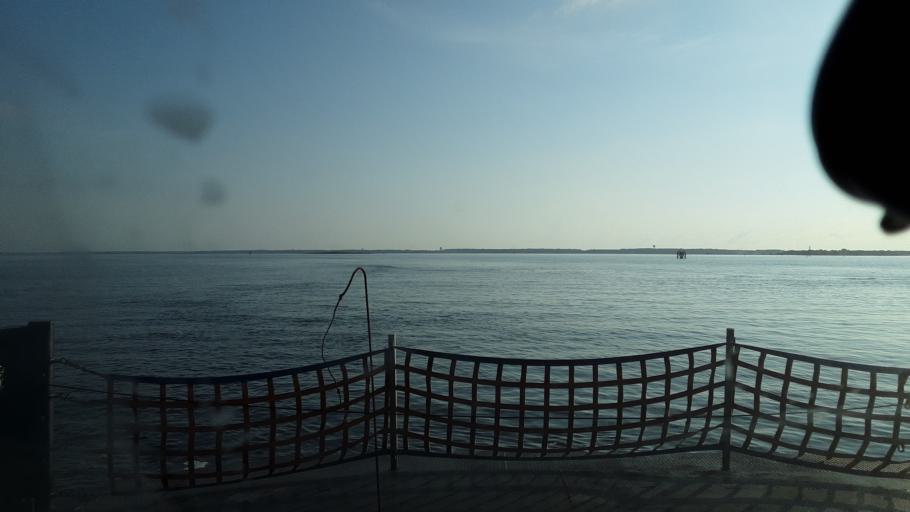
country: US
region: North Carolina
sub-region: New Hanover County
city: Kure Beach
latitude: 33.9593
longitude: -77.9544
